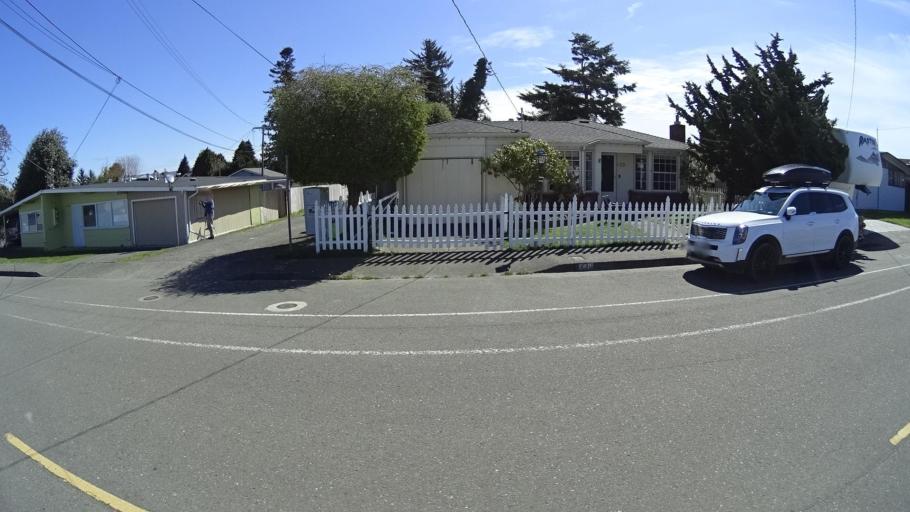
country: US
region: California
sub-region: Humboldt County
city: Myrtletown
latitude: 40.7909
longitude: -124.1263
